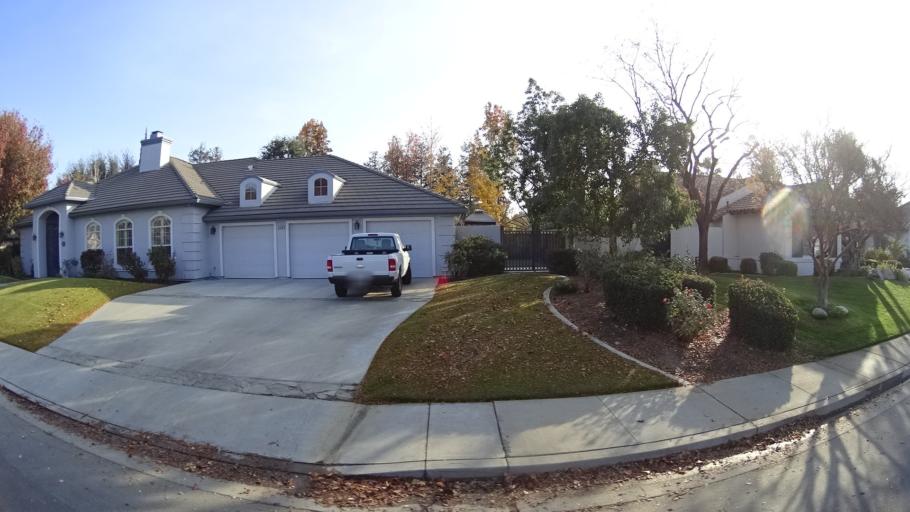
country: US
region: California
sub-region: Kern County
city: Rosedale
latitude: 35.3704
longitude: -119.1412
